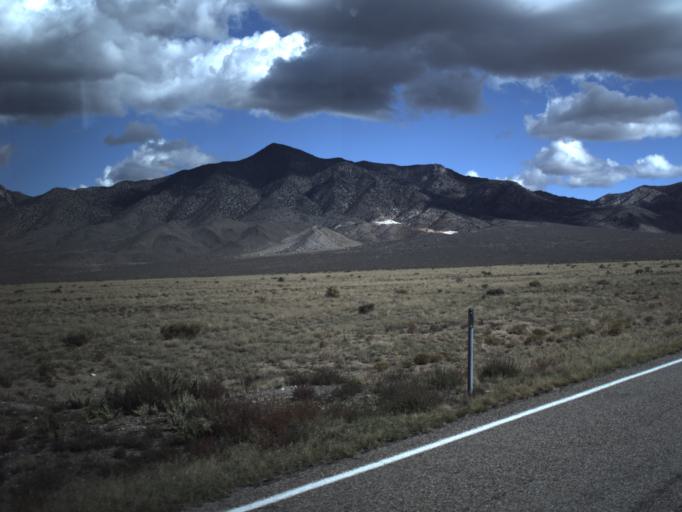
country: US
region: Utah
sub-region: Beaver County
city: Milford
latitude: 38.4543
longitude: -113.3573
